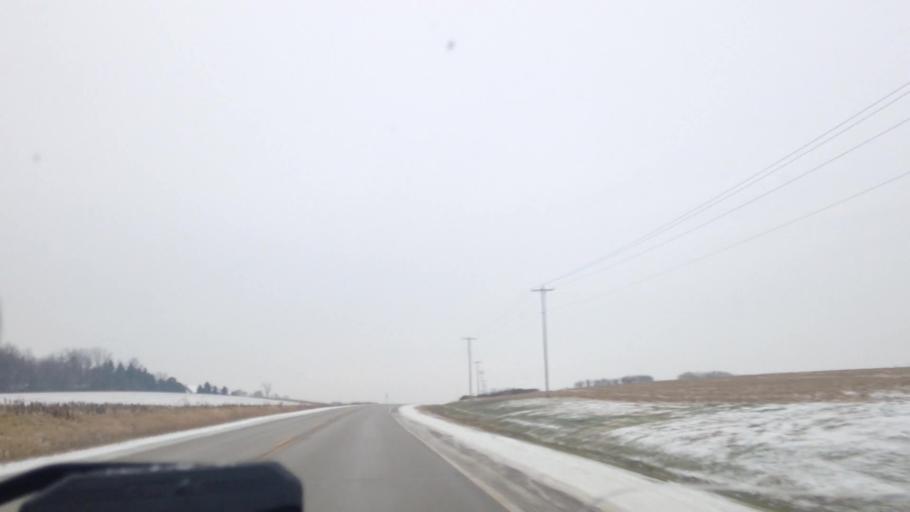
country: US
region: Wisconsin
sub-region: Dodge County
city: Hustisford
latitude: 43.3575
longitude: -88.5169
